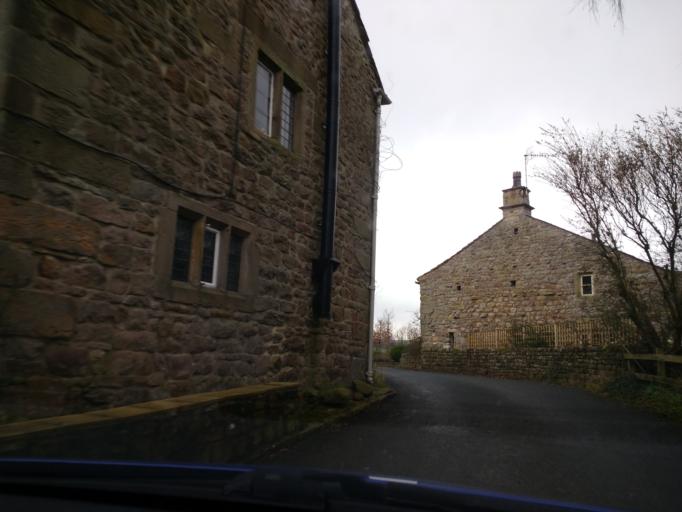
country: GB
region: England
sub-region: Lancashire
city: Caton
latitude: 54.0820
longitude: -2.7413
